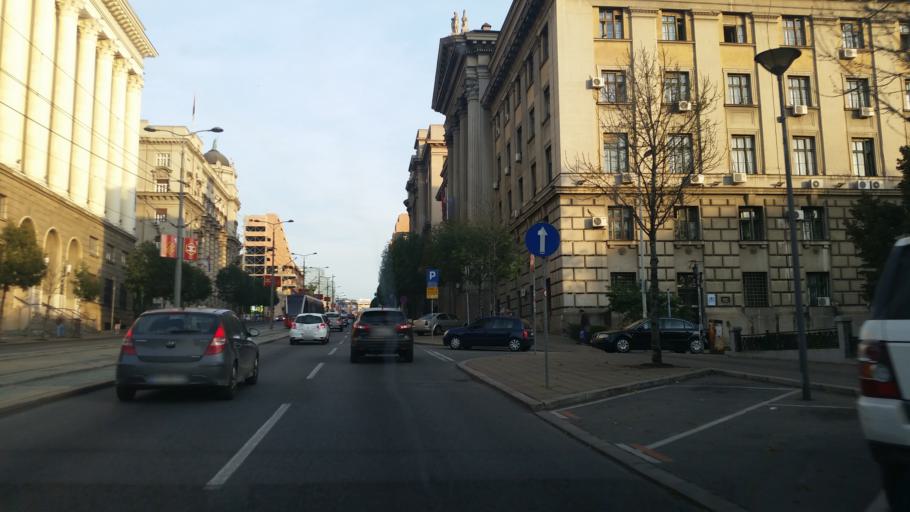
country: RS
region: Central Serbia
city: Belgrade
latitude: 44.8068
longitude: 20.4583
